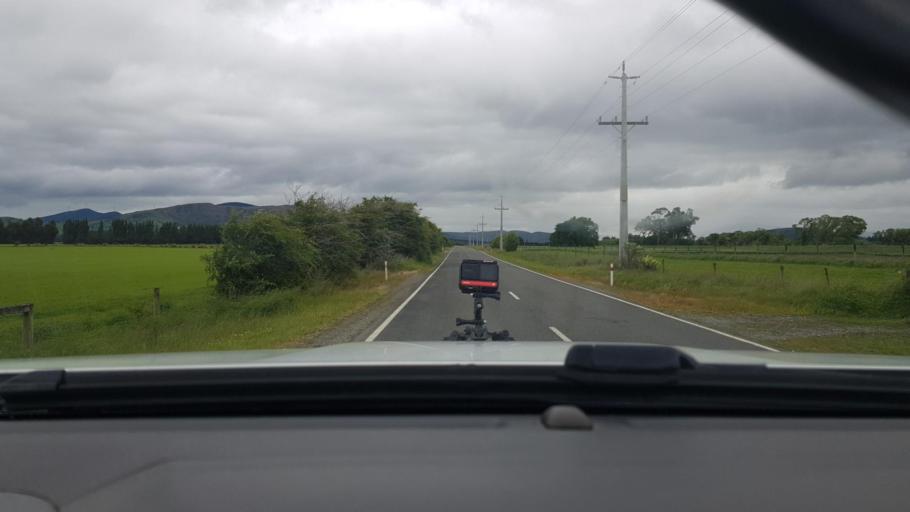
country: NZ
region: Southland
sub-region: Southland District
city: Winton
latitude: -45.8722
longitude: 168.3577
